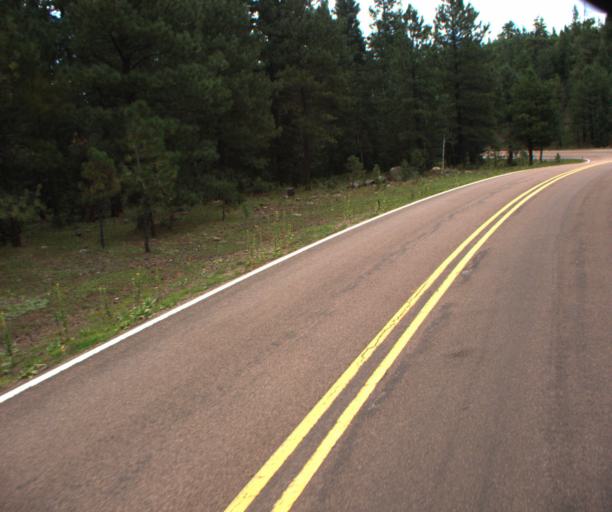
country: US
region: Arizona
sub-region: Navajo County
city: Pinetop-Lakeside
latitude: 34.0037
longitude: -109.7558
